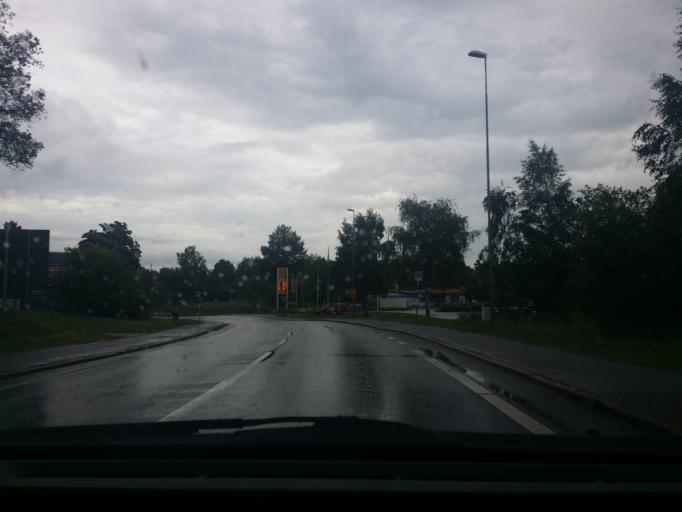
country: SE
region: OErebro
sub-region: Lindesbergs Kommun
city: Frovi
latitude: 59.4653
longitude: 15.3669
